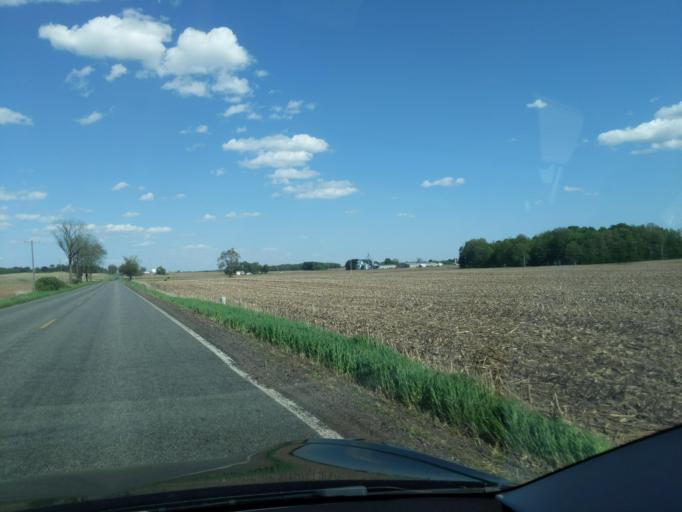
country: US
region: Michigan
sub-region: Kent County
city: Lowell
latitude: 42.7988
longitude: -85.3047
